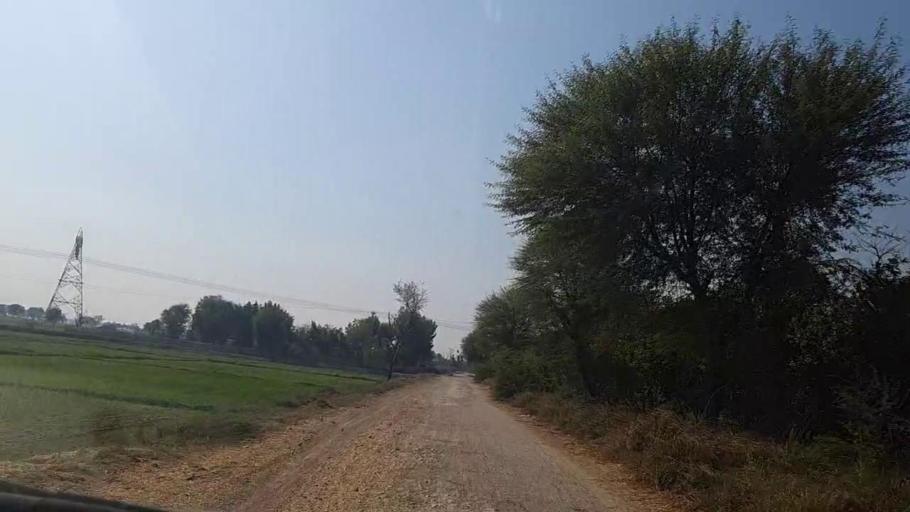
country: PK
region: Sindh
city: Sakrand
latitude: 26.0253
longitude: 68.3786
